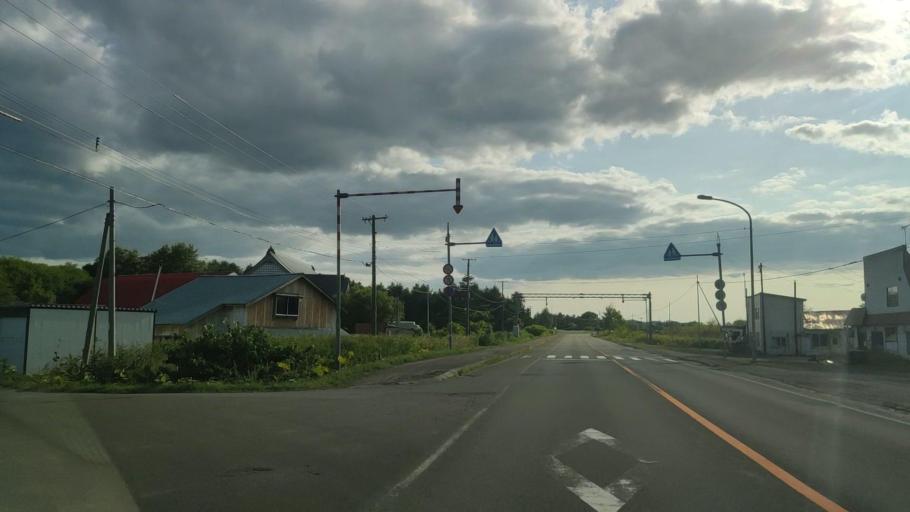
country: JP
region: Hokkaido
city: Makubetsu
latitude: 44.8989
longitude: 141.9315
